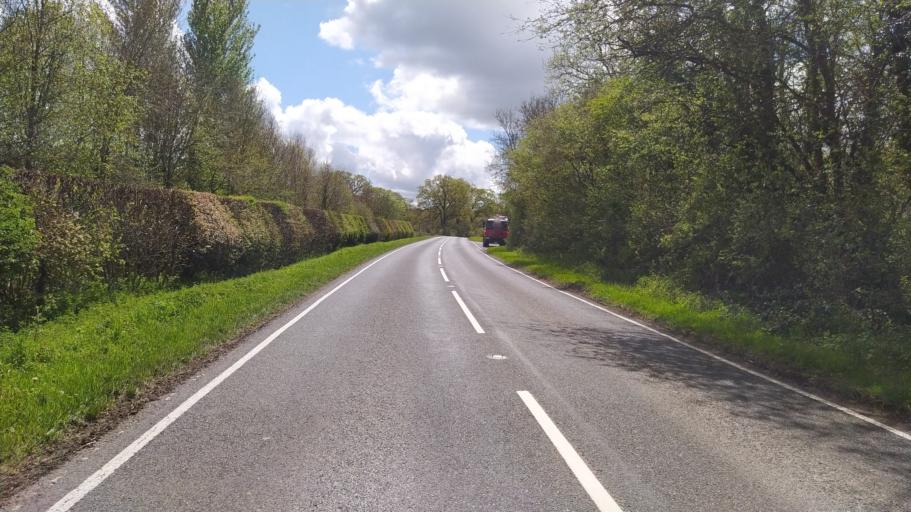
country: GB
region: England
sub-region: Somerset
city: Frome
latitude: 51.1838
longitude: -2.3137
